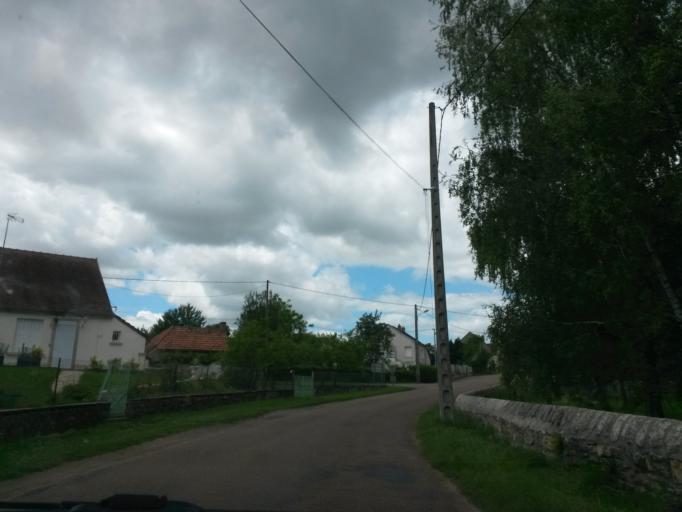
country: FR
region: Bourgogne
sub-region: Departement de la Nievre
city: La Charite-sur-Loire
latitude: 47.2309
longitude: 3.0654
